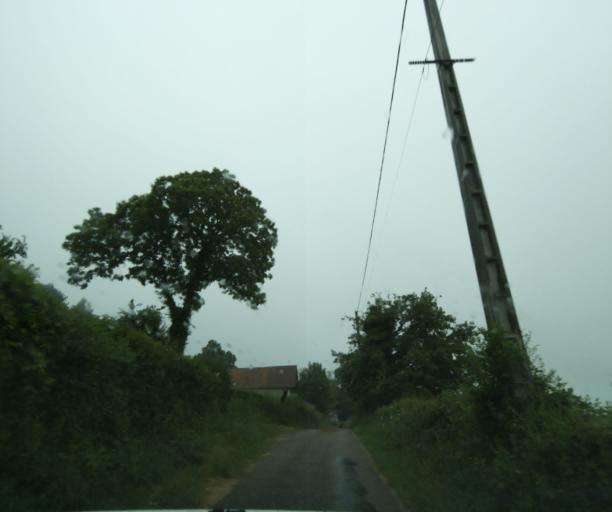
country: FR
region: Bourgogne
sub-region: Departement de Saone-et-Loire
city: La Clayette
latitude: 46.3659
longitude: 4.3504
